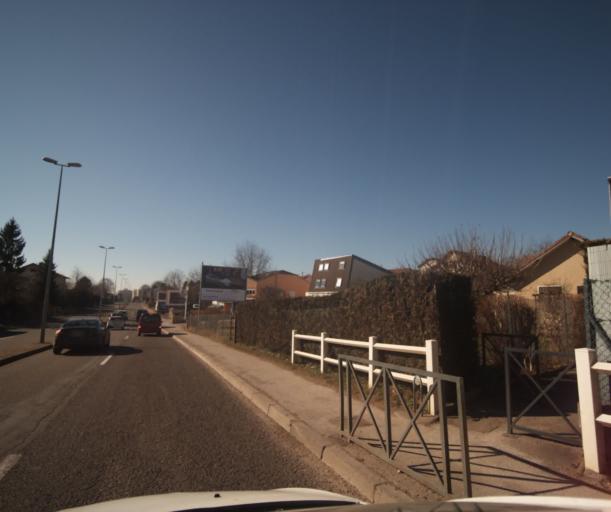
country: FR
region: Franche-Comte
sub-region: Departement du Doubs
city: Besancon
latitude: 47.2612
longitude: 6.0344
